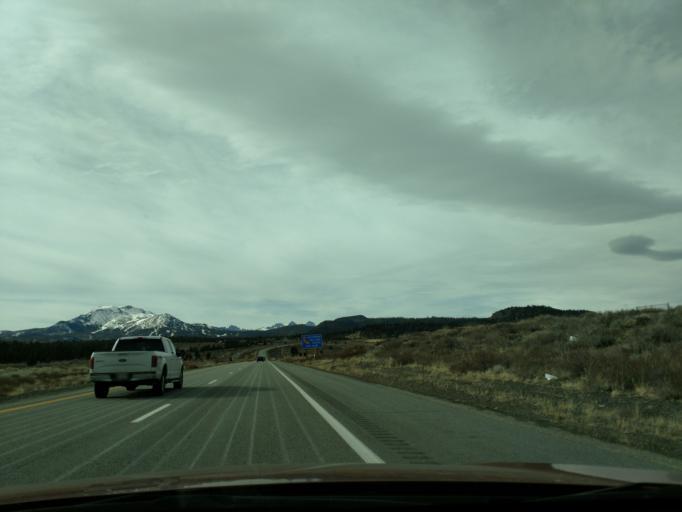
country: US
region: California
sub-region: Mono County
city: Mammoth Lakes
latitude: 37.6376
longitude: -118.8994
